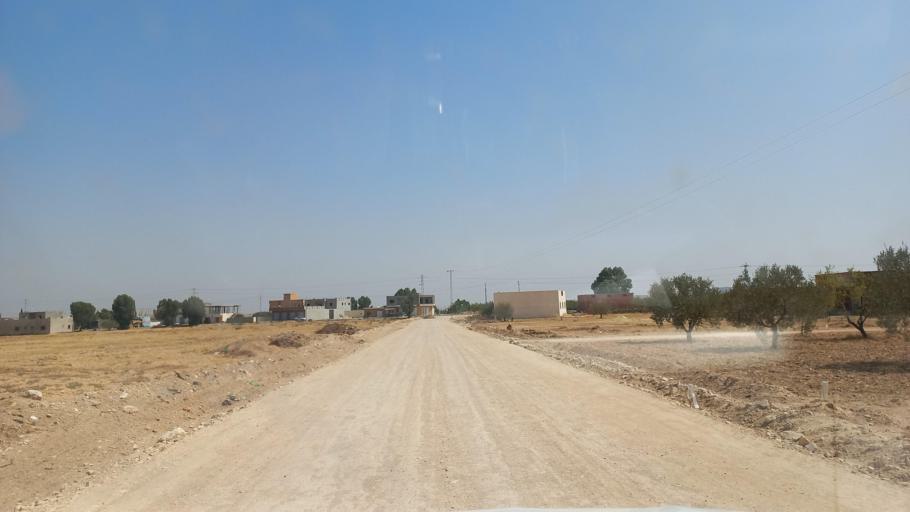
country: TN
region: Al Qasrayn
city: Kasserine
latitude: 35.2554
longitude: 9.0153
